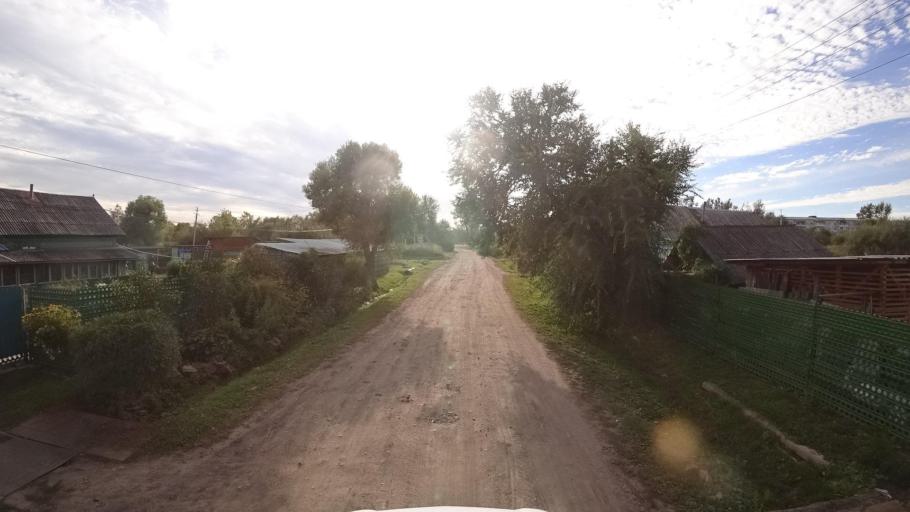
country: RU
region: Primorskiy
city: Dostoyevka
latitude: 44.2897
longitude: 133.4284
